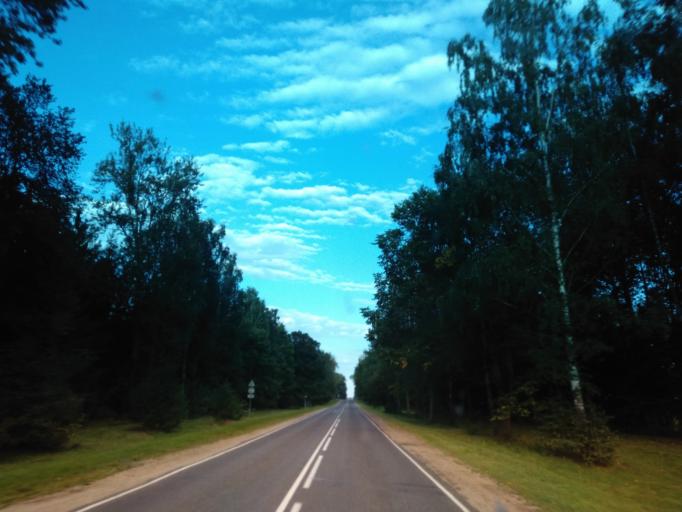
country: BY
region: Minsk
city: Uzda
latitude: 53.4400
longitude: 27.2927
